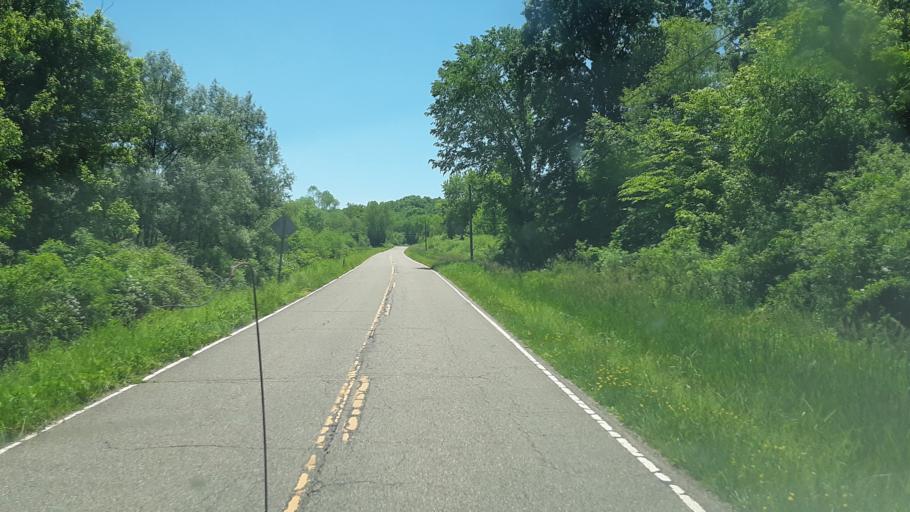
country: US
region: Ohio
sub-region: Coshocton County
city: Coshocton
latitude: 40.2959
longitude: -82.0071
